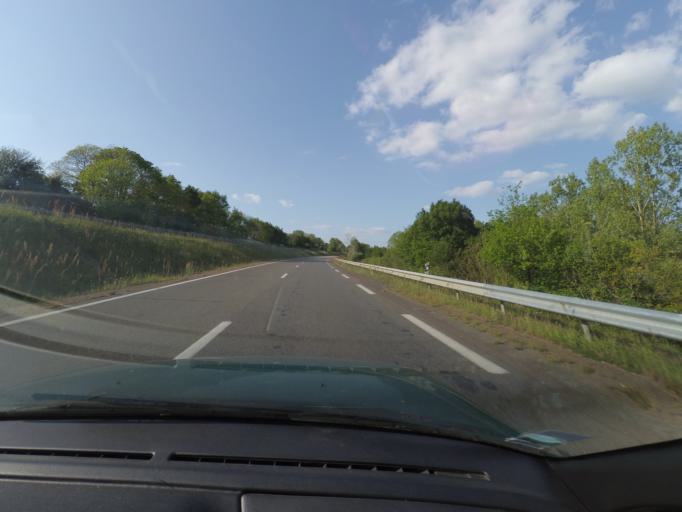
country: FR
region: Pays de la Loire
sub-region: Departement de la Vendee
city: Saligny
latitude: 46.8240
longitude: -1.4286
